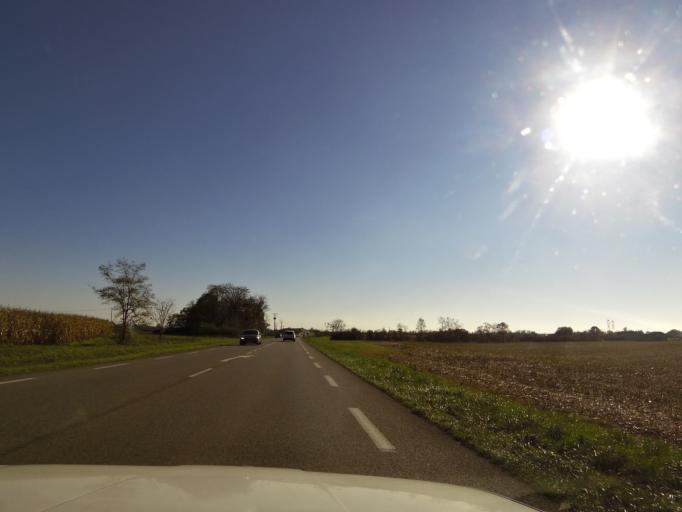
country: FR
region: Rhone-Alpes
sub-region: Departement de l'Ain
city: Perouges
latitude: 45.8692
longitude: 5.1821
